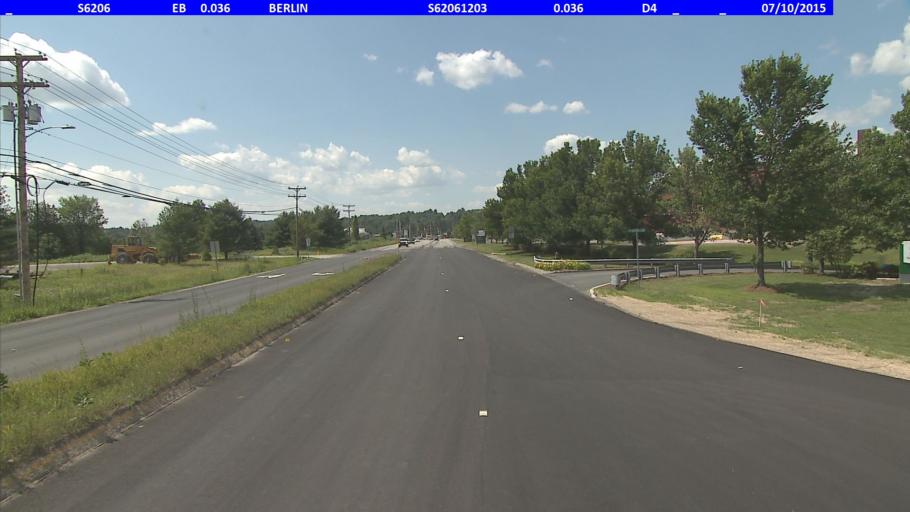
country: US
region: Vermont
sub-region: Washington County
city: Montpelier
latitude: 44.2187
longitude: -72.5601
